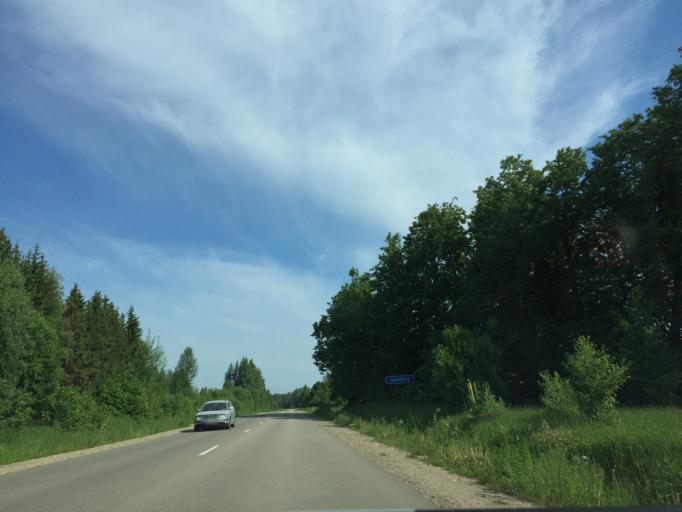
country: LV
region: Rezekne
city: Rezekne
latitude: 56.4570
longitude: 27.3823
